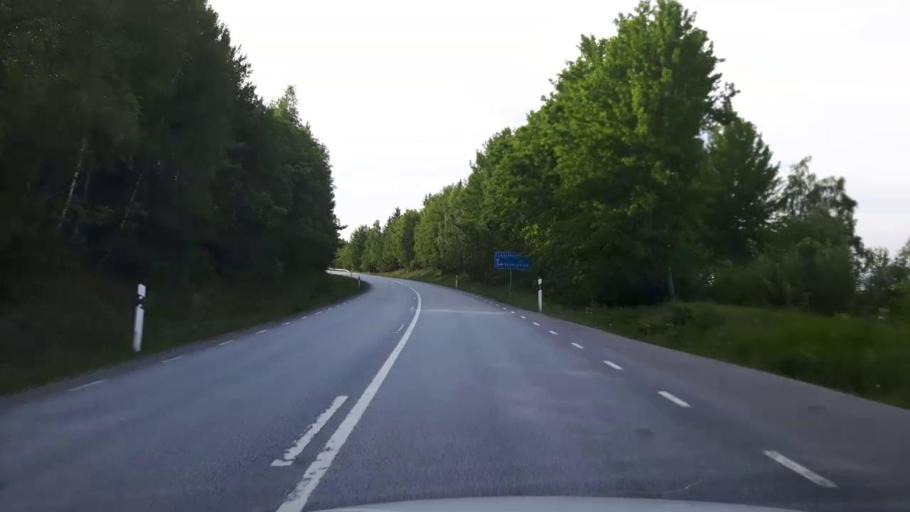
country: SE
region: Uppsala
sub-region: Habo Kommun
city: Balsta
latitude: 59.6501
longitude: 17.5623
